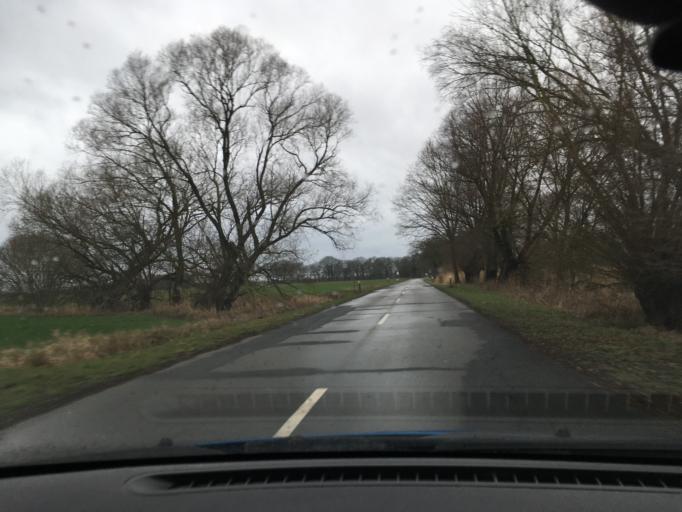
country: DE
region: Mecklenburg-Vorpommern
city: Nostorf
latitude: 53.3606
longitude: 10.6460
